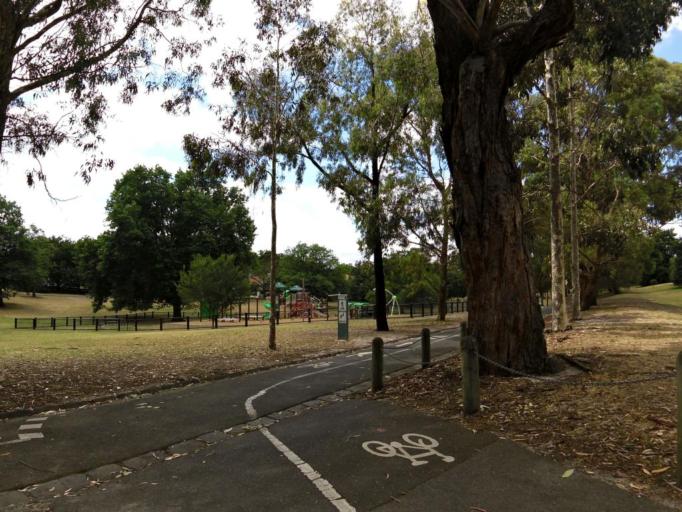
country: AU
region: Victoria
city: Balwyn
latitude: -37.8227
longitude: 145.0678
